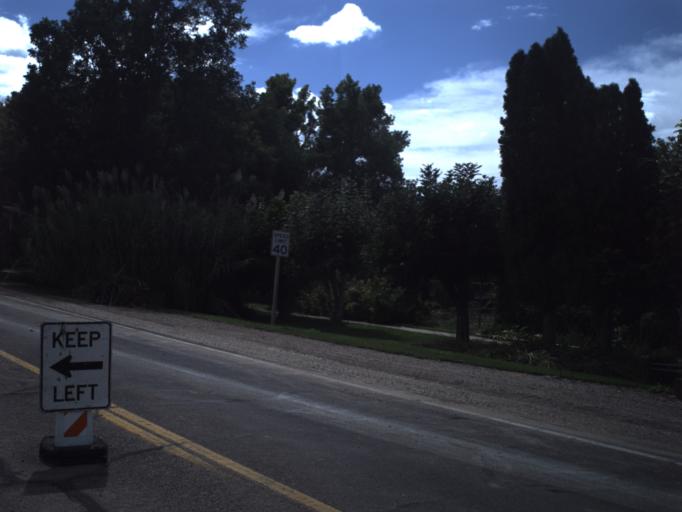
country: US
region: Utah
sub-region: Millard County
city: Fillmore
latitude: 38.9769
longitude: -112.3237
